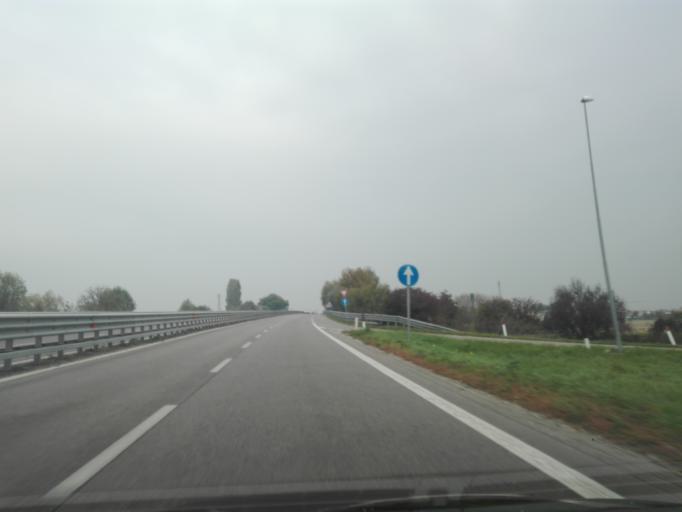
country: IT
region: Veneto
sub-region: Provincia di Verona
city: Villa Bartolomea
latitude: 45.1637
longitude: 11.3039
